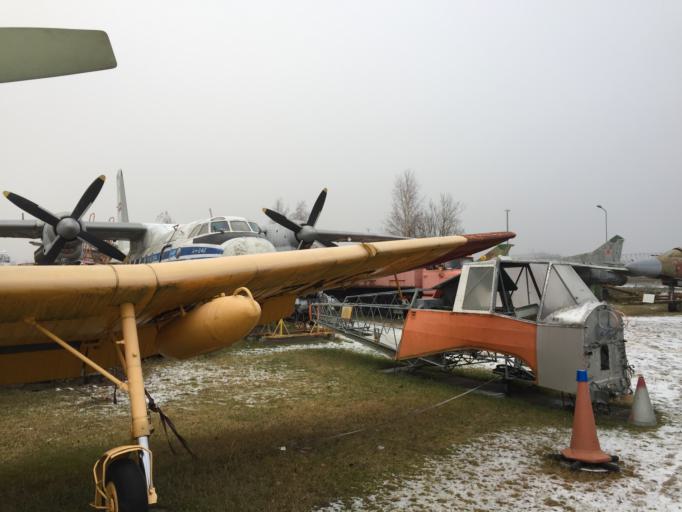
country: LV
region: Babite
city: Pinki
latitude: 56.9256
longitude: 23.9806
